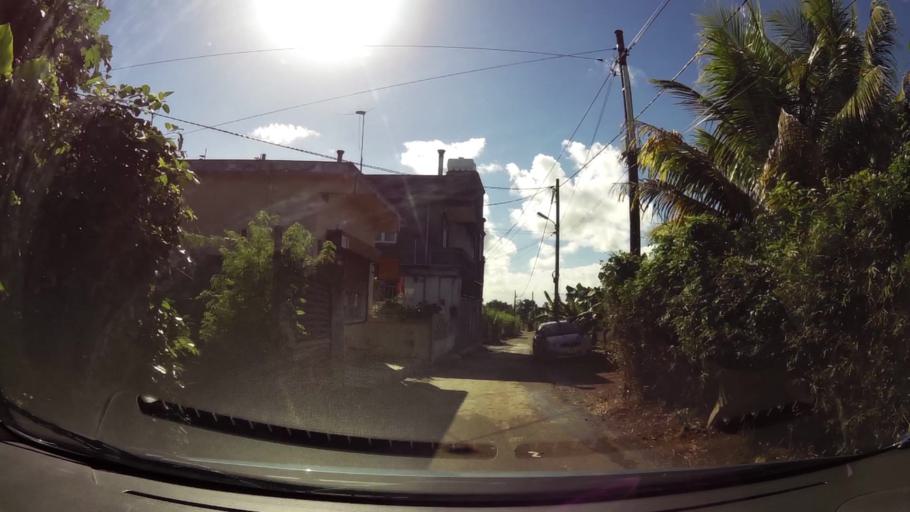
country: MU
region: Grand Port
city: Mahebourg
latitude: -20.3992
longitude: 57.6944
